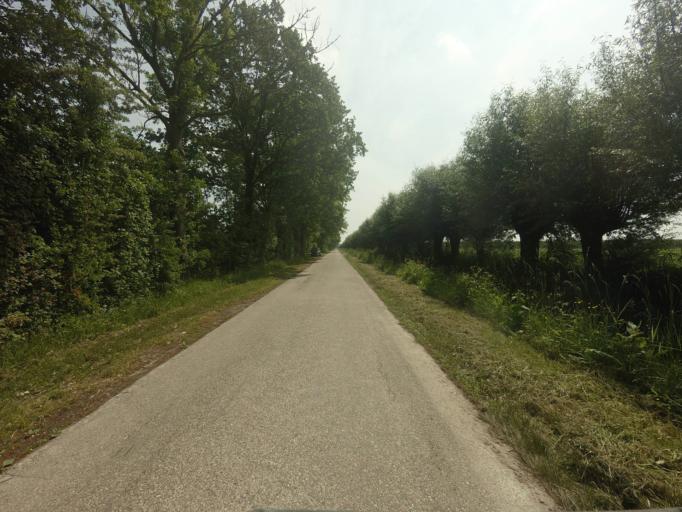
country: NL
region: Gelderland
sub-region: Gemeente Culemborg
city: Culemborg
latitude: 51.9946
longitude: 5.2237
